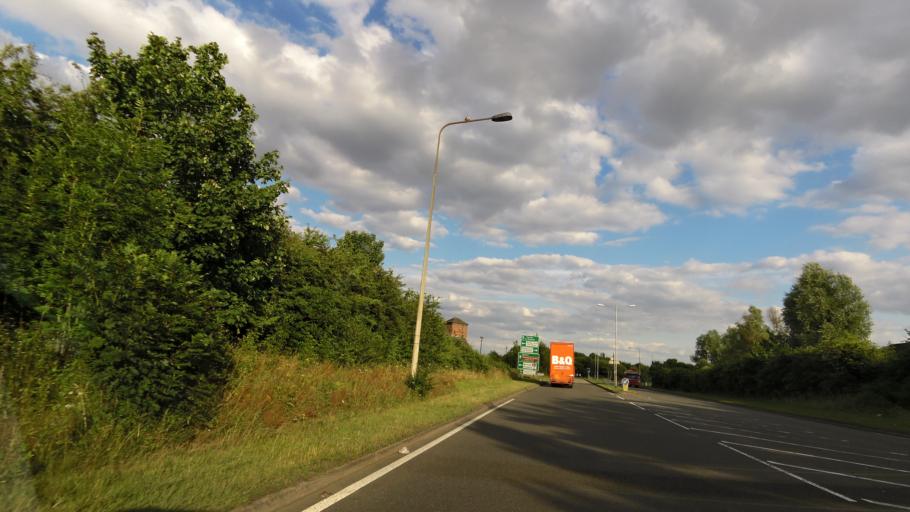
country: GB
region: England
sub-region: Nottinghamshire
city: Worksop
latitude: 53.3120
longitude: -1.1453
